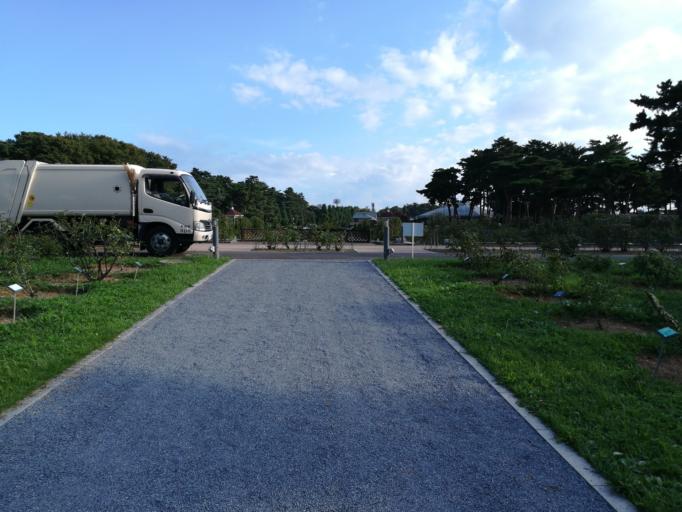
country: JP
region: Gunma
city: Maebashi-shi
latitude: 36.4204
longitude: 139.0489
